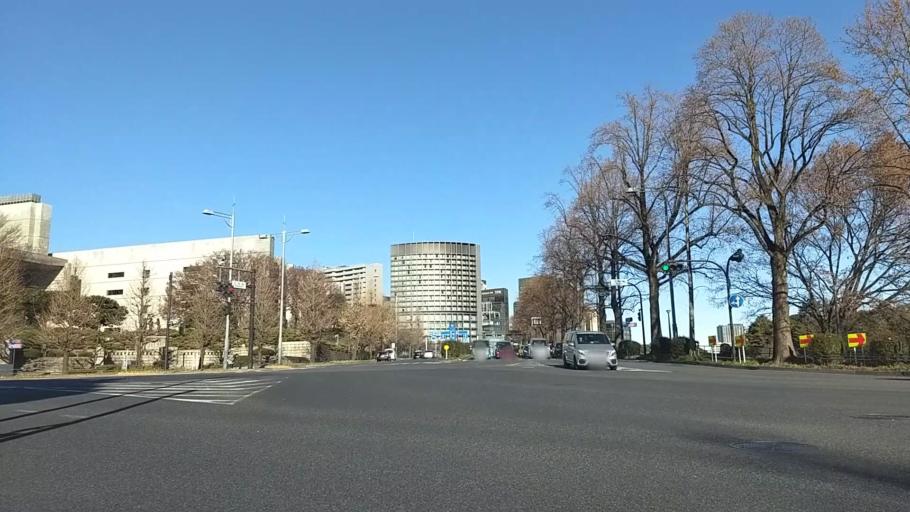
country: JP
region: Tokyo
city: Tokyo
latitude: 35.6796
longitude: 139.7461
